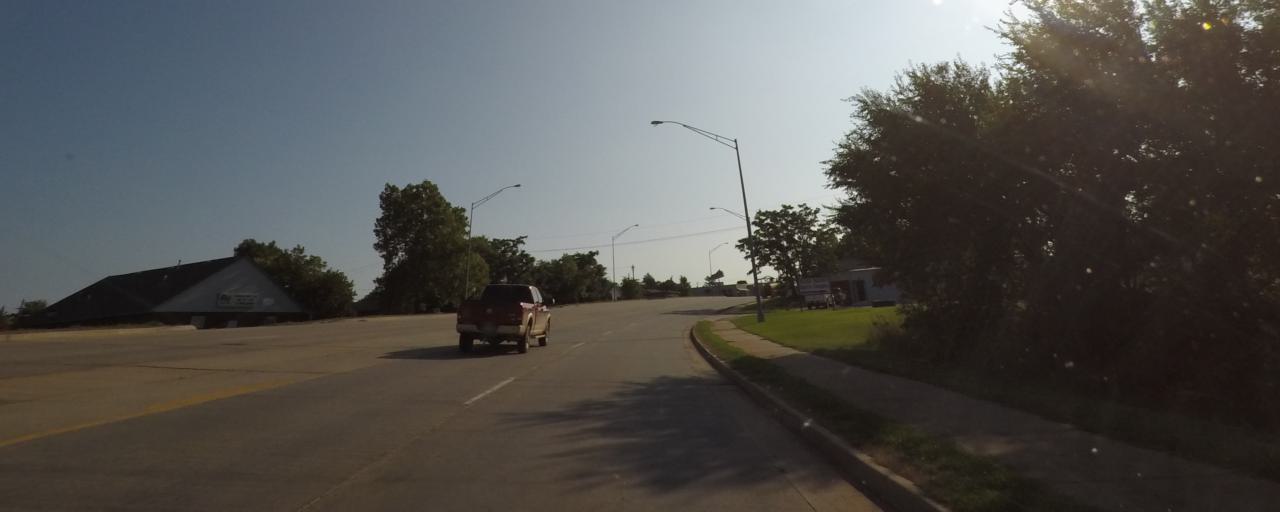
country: US
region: Oklahoma
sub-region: McClain County
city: Blanchard
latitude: 35.1375
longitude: -97.6627
